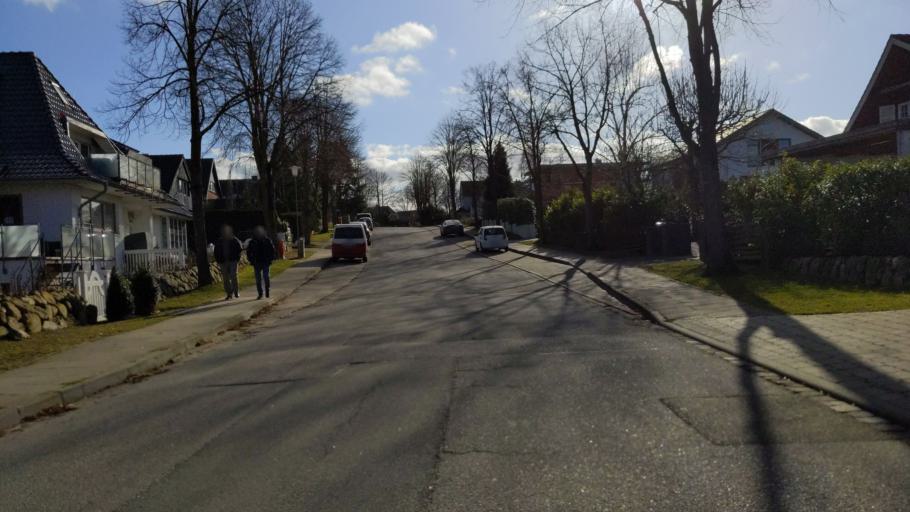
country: DE
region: Schleswig-Holstein
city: Scharbeutz
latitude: 54.0179
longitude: 10.7578
